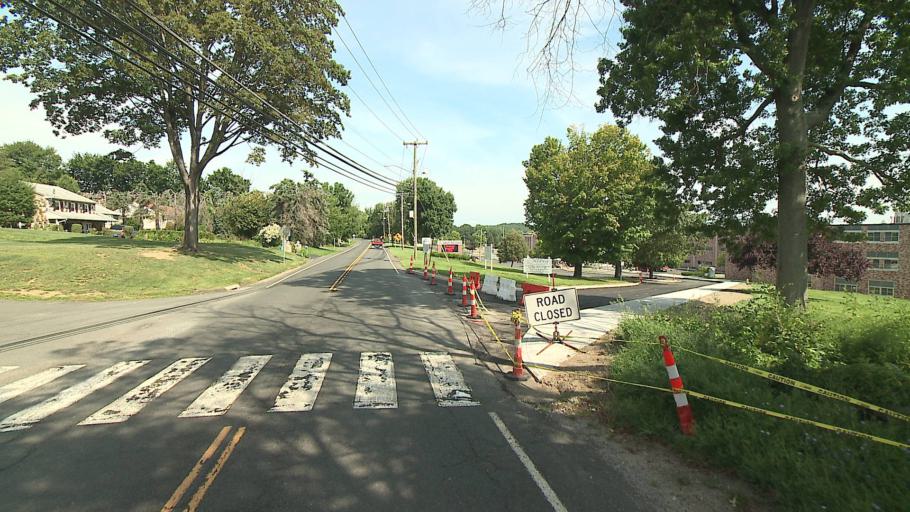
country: US
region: Connecticut
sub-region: Fairfield County
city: Danbury
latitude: 41.4150
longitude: -73.4717
